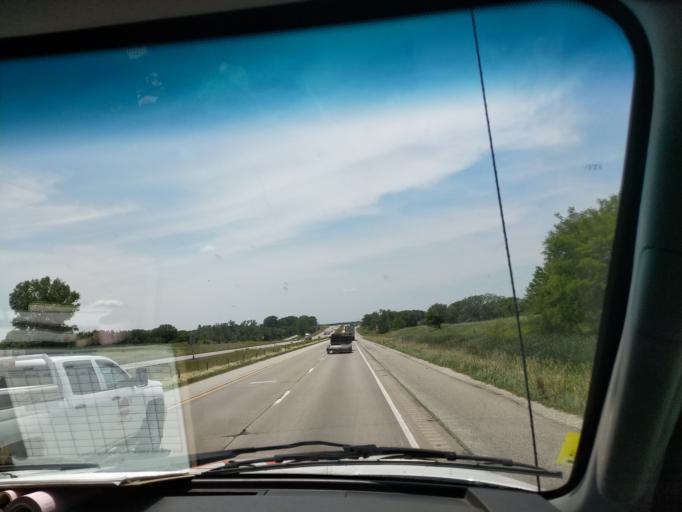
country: US
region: Iowa
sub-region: Dallas County
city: Waukee
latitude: 41.5775
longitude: -93.8379
